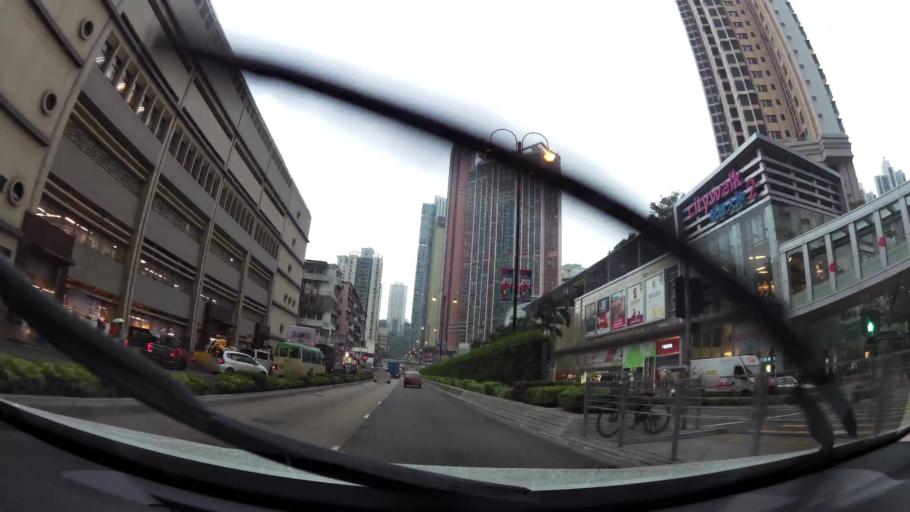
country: HK
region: Tsuen Wan
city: Tsuen Wan
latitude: 22.3690
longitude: 114.1140
